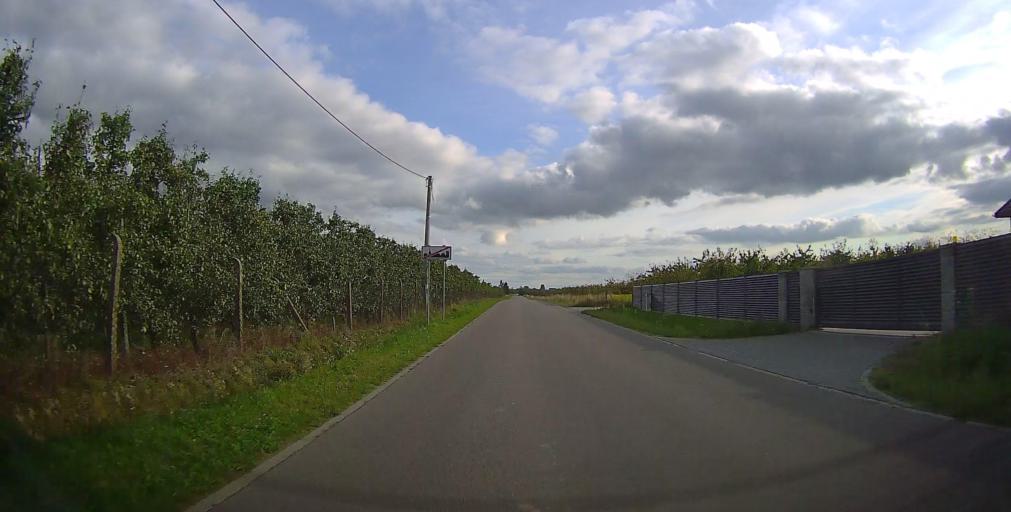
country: PL
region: Masovian Voivodeship
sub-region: Powiat grojecki
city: Jasieniec
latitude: 51.7523
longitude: 20.9620
